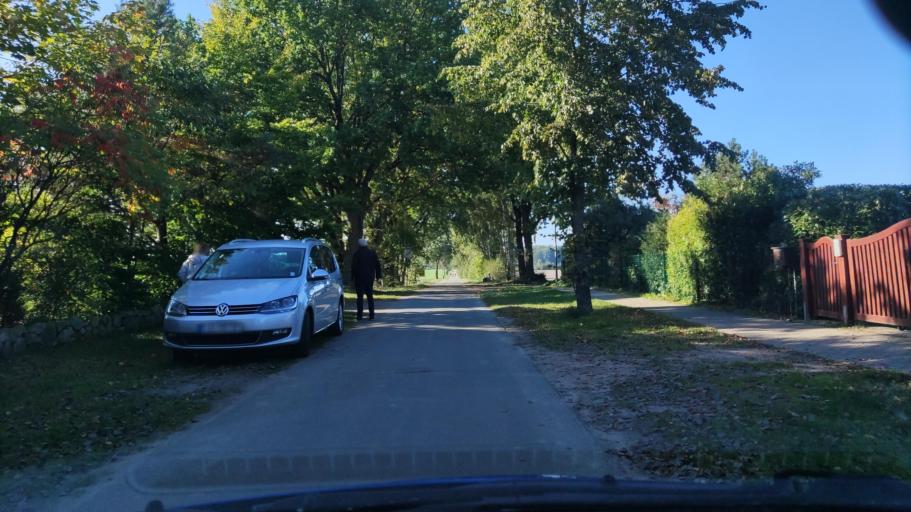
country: DE
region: Lower Saxony
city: Sudergellersen
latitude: 53.2115
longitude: 10.2888
